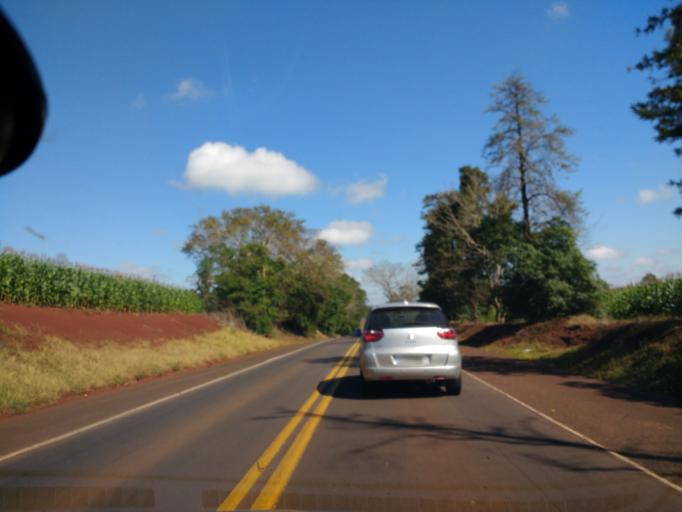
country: BR
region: Parana
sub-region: Cianorte
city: Cianorte
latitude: -23.6521
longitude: -52.4944
